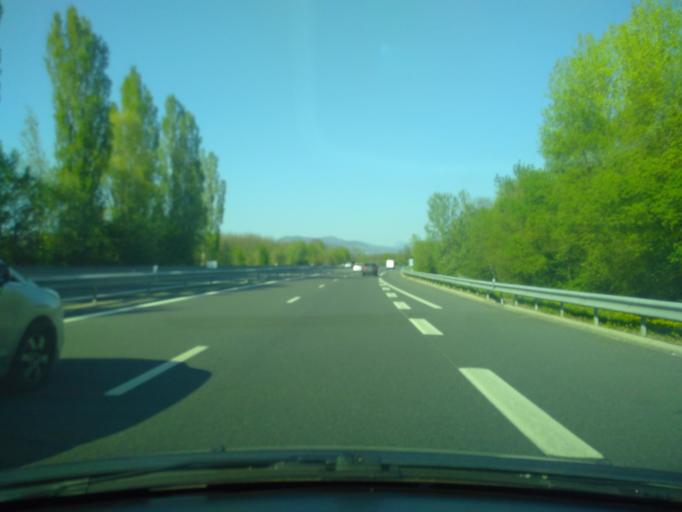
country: FR
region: Rhone-Alpes
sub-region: Departement de l'Isere
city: Saint-Quentin-sur-Isere
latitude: 45.2891
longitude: 5.5266
